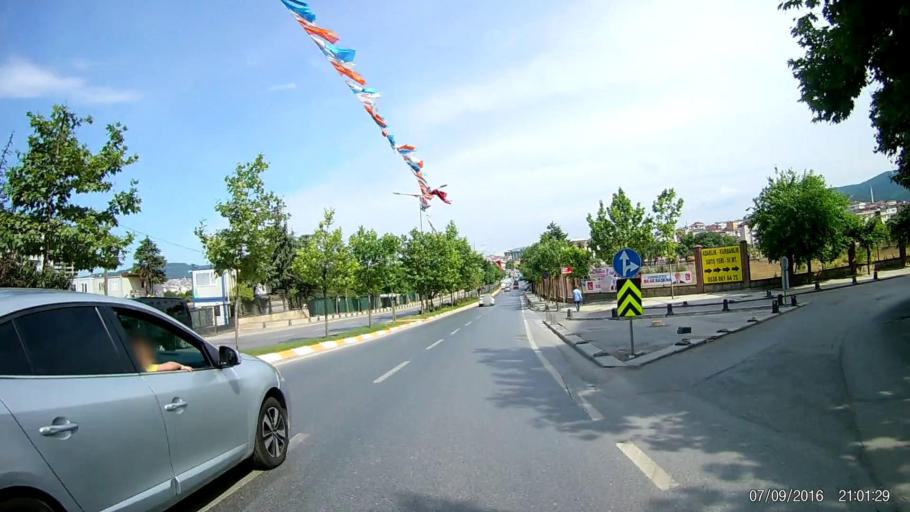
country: TR
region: Istanbul
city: Sultanbeyli
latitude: 40.9737
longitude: 29.2455
